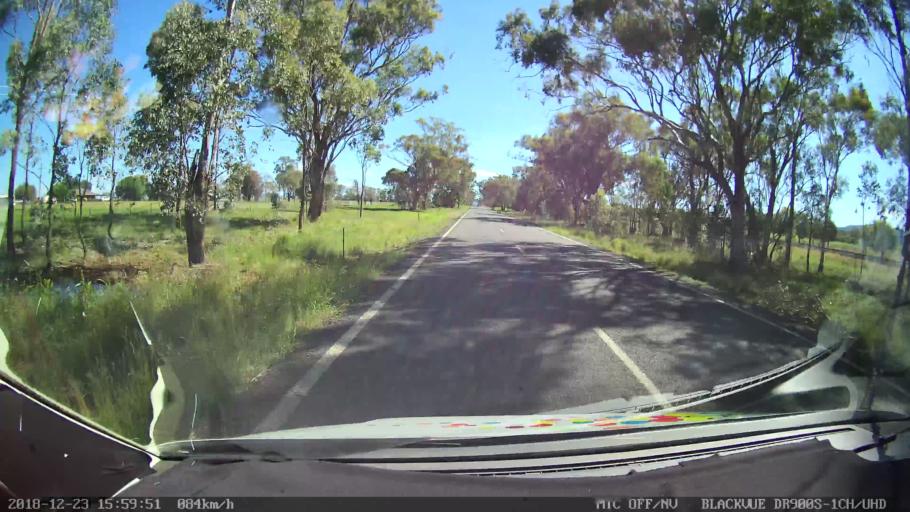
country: AU
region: New South Wales
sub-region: Tamworth Municipality
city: Phillip
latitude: -31.2042
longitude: 150.8299
